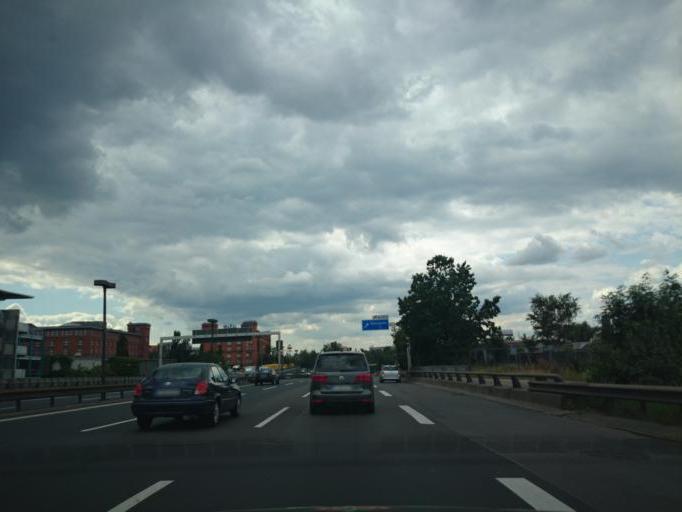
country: DE
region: Berlin
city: Tempelhof Bezirk
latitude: 52.4701
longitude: 13.3785
